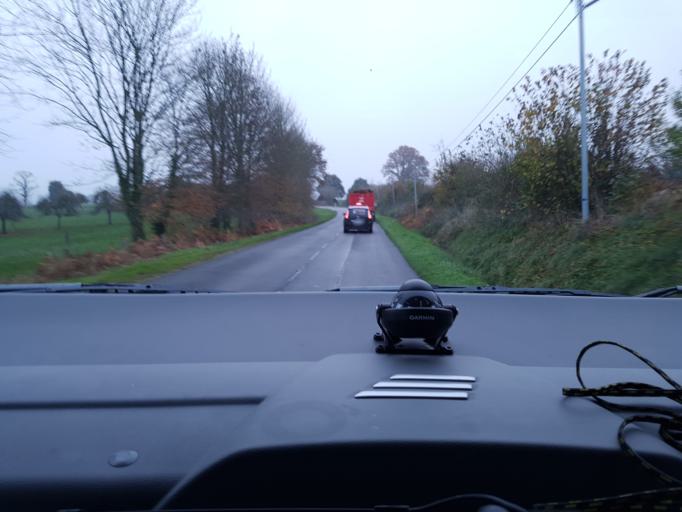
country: FR
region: Brittany
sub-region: Departement d'Ille-et-Vilaine
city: Antrain
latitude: 48.4582
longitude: -1.4286
